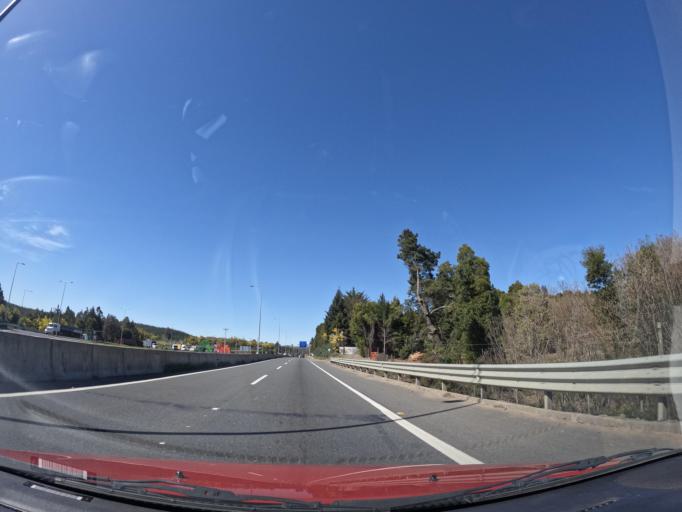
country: CL
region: Biobio
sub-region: Provincia de Concepcion
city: Chiguayante
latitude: -36.9050
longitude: -72.7865
